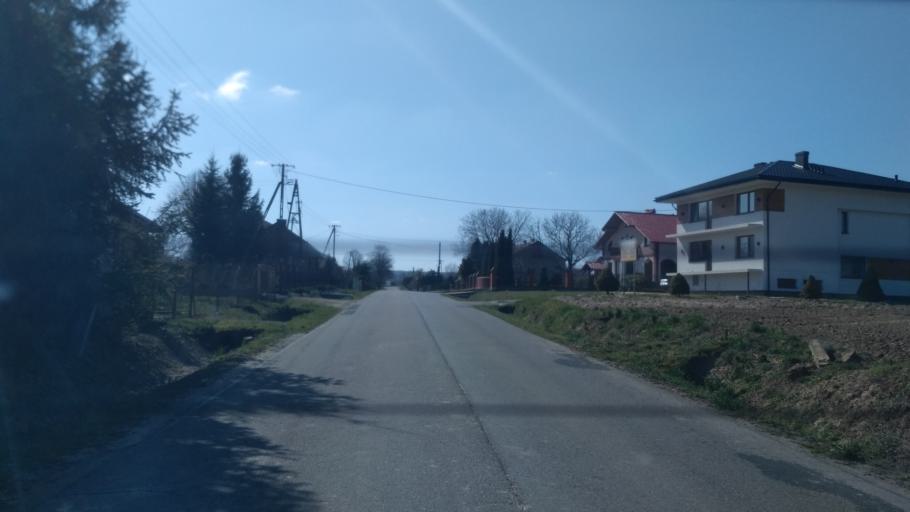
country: PL
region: Subcarpathian Voivodeship
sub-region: Powiat przeworski
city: Pantalowice
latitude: 49.9343
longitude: 22.4446
